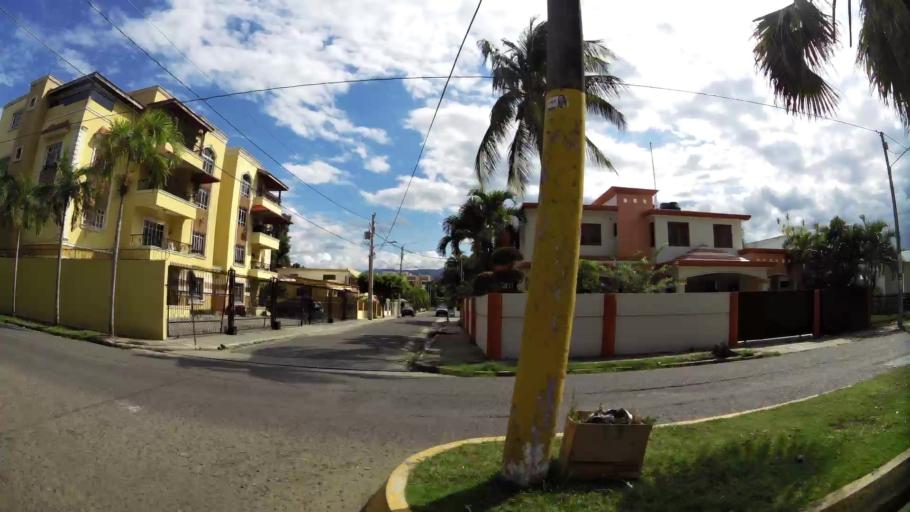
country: DO
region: La Vega
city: Concepcion de La Vega
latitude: 19.2195
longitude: -70.5262
